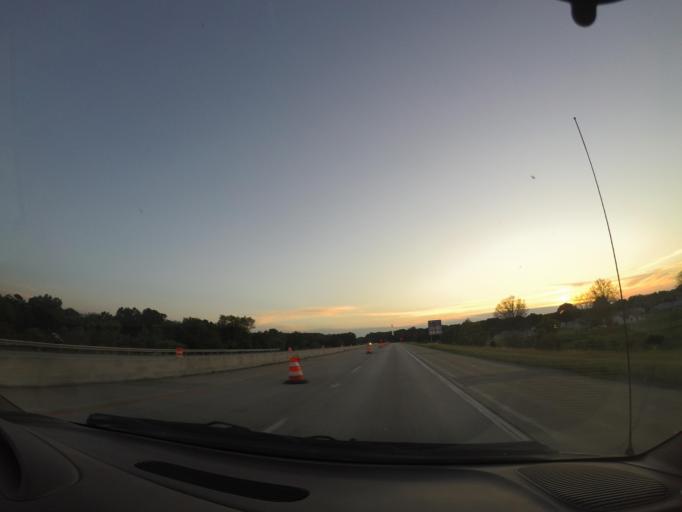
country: US
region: Indiana
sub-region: Elkhart County
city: Dunlap
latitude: 41.6571
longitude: -85.9226
